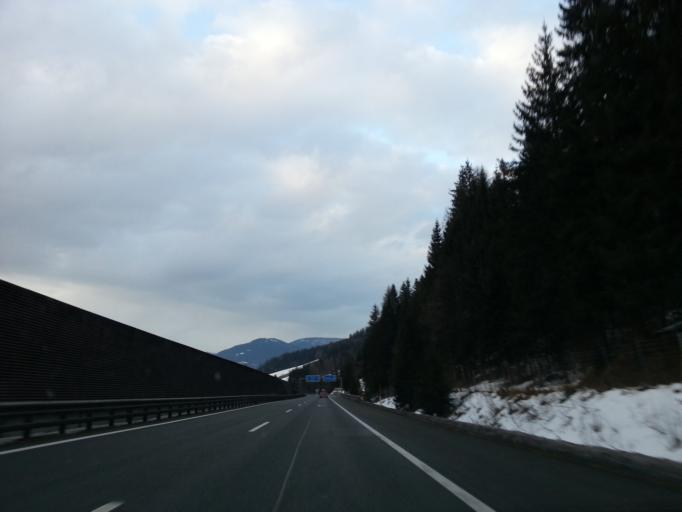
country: AT
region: Salzburg
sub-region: Politischer Bezirk Sankt Johann im Pongau
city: Flachau
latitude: 47.3546
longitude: 13.3974
